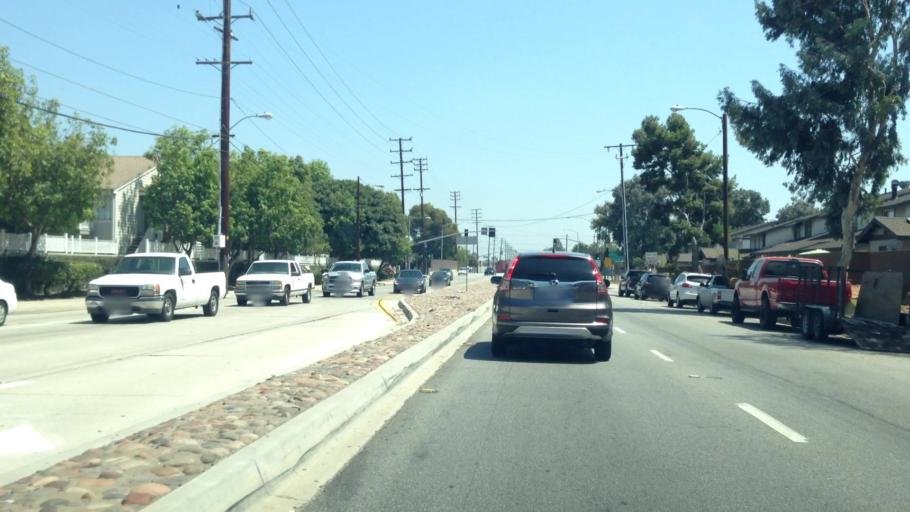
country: US
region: California
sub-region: Los Angeles County
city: West Carson
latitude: 33.8244
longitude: -118.2897
